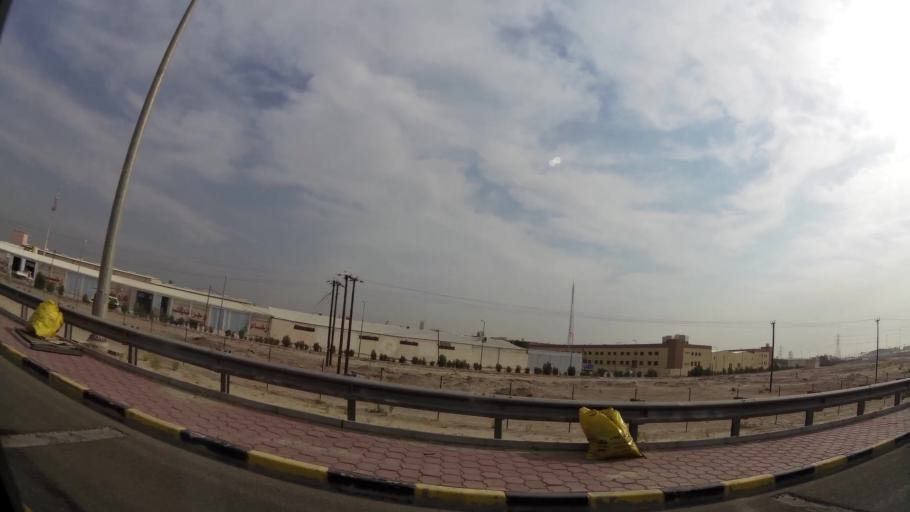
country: KW
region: Muhafazat al Jahra'
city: Al Jahra'
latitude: 29.2970
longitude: 47.7372
